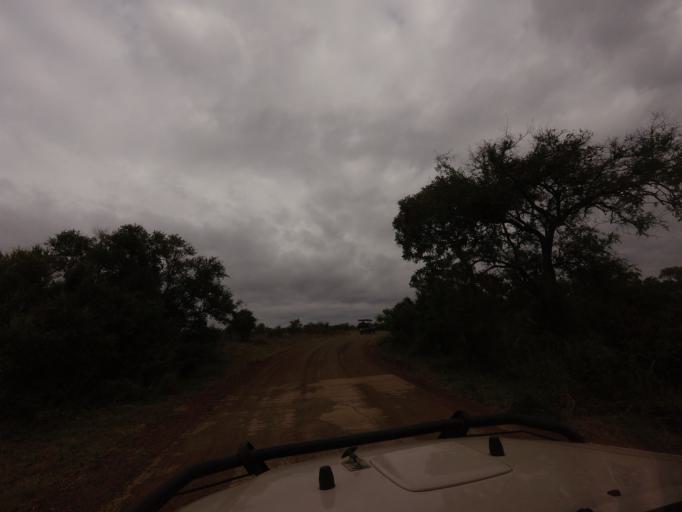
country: ZA
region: Mpumalanga
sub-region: Ehlanzeni District
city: Komatipoort
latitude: -25.1642
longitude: 31.9365
